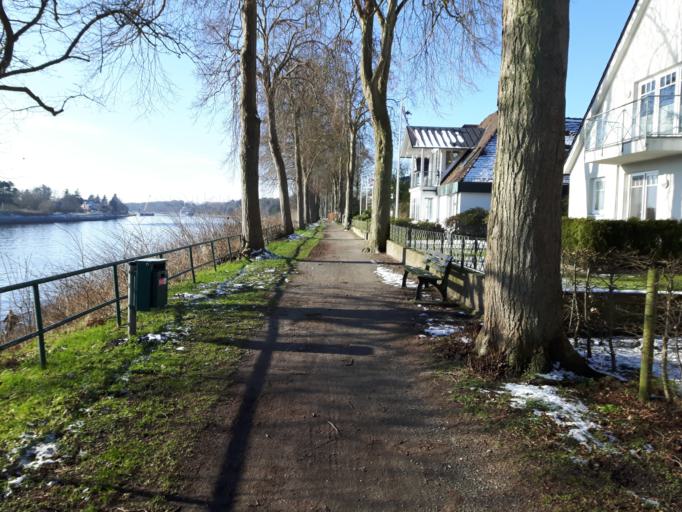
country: DE
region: Schleswig-Holstein
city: Westerronfeld
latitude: 54.2909
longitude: 9.6613
